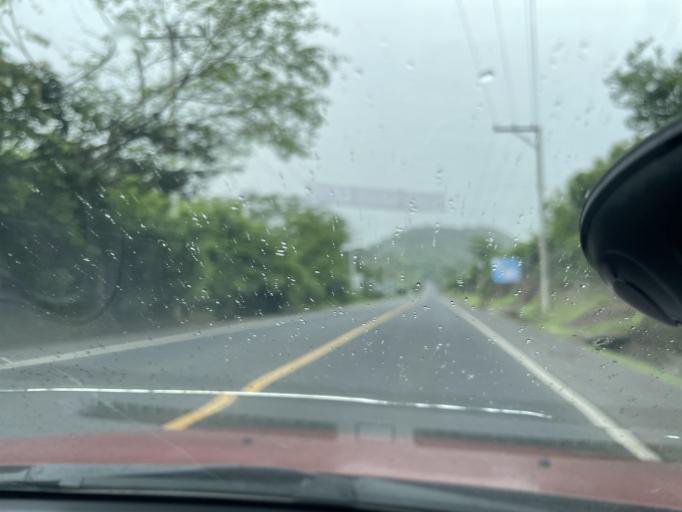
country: SV
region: San Miguel
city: San Miguel
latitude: 13.5251
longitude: -88.1444
